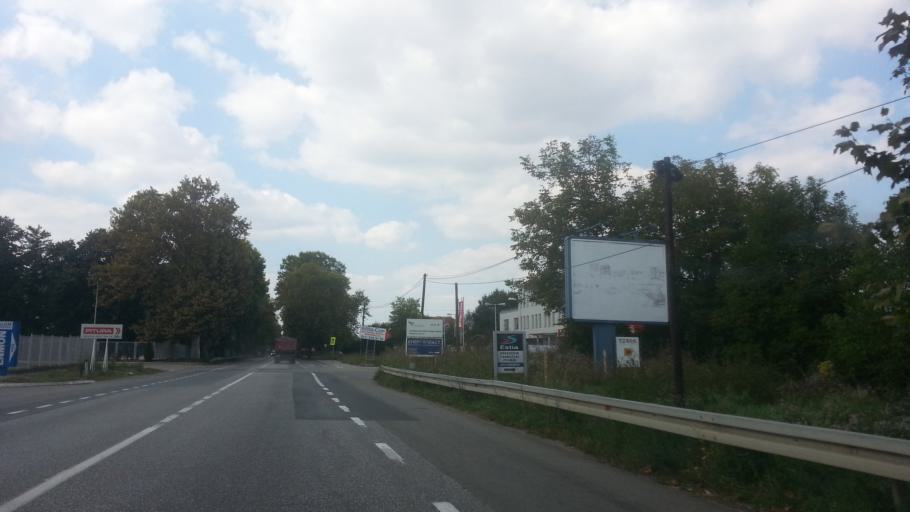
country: RS
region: Central Serbia
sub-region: Belgrade
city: Zemun
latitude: 44.8669
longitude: 20.3601
